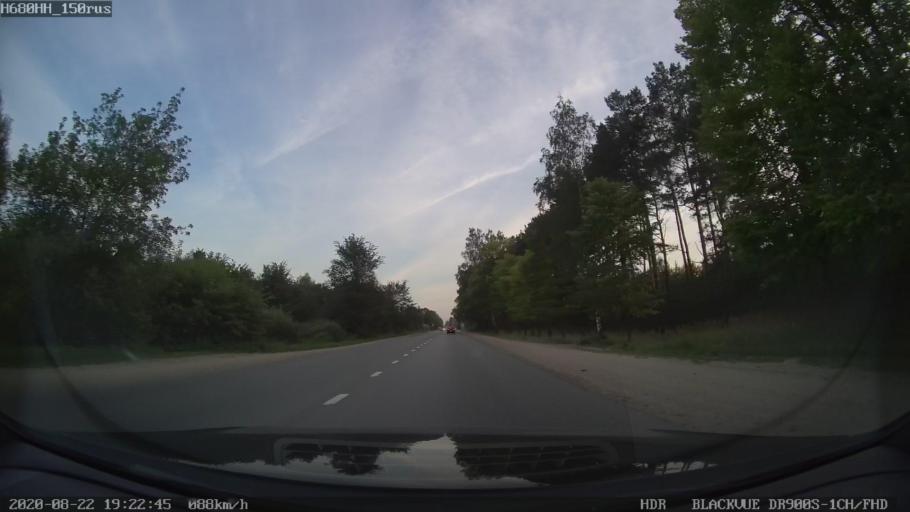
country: RU
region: Tverskaya
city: Tver
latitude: 56.9008
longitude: 35.9323
